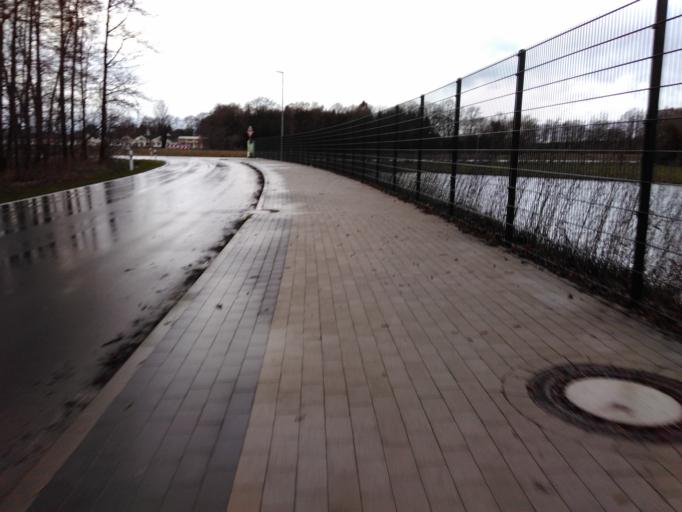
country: DE
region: North Rhine-Westphalia
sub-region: Regierungsbezirk Detmold
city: Verl
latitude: 51.8814
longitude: 8.4786
